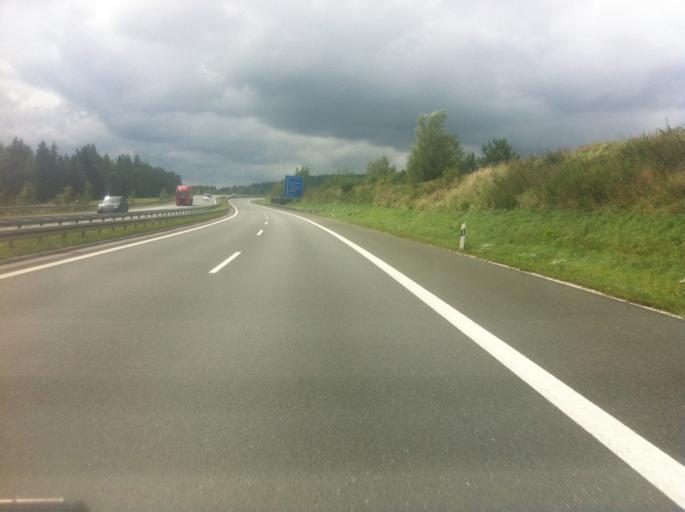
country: DE
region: Bavaria
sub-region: Upper Palatinate
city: Leuchtenberg
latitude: 49.5839
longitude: 12.2787
